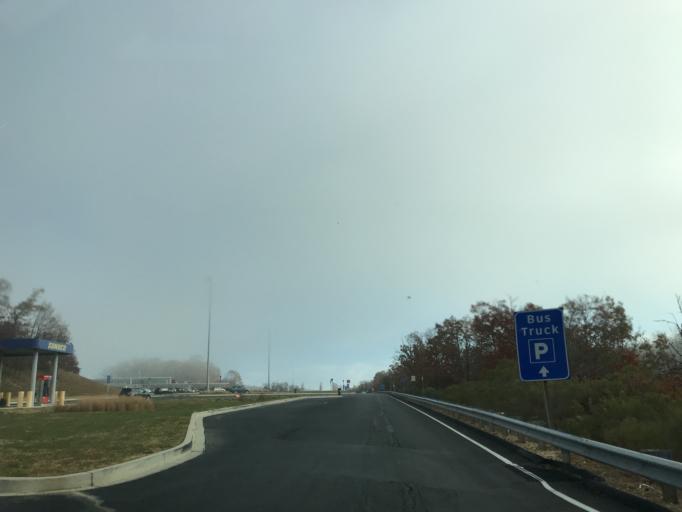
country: US
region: Maryland
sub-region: Cecil County
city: Charlestown
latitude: 39.6099
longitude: -76.0110
